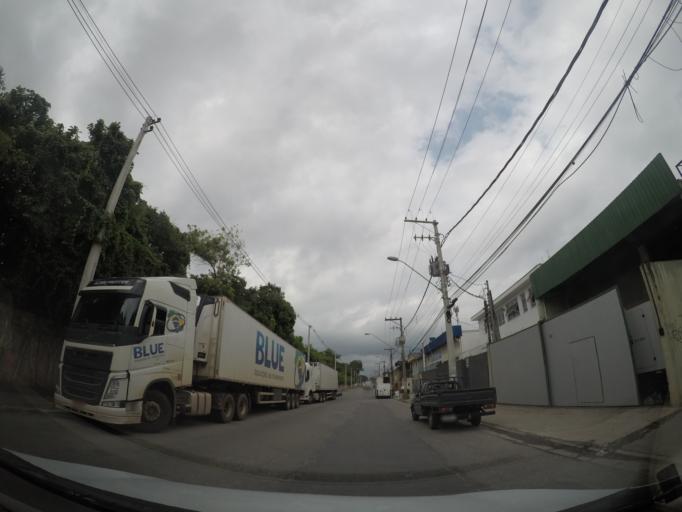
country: BR
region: Sao Paulo
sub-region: Aruja
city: Aruja
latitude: -23.4077
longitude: -46.4085
